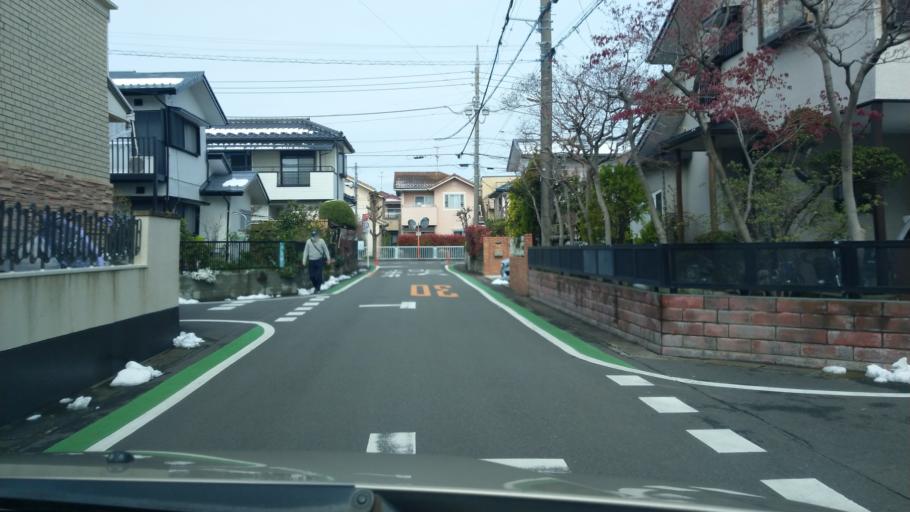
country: JP
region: Saitama
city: Yono
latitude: 35.9092
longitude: 139.5774
